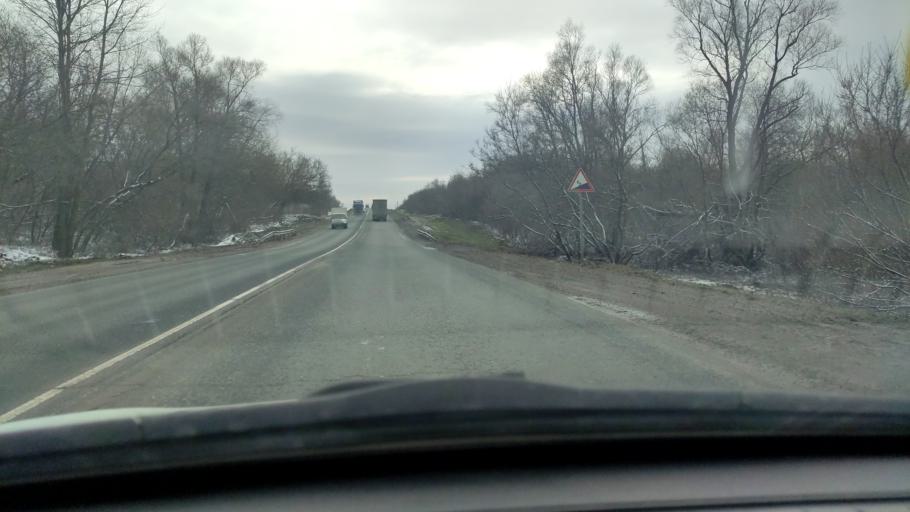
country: RU
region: Samara
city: Zhigulevsk
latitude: 53.3537
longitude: 49.4544
